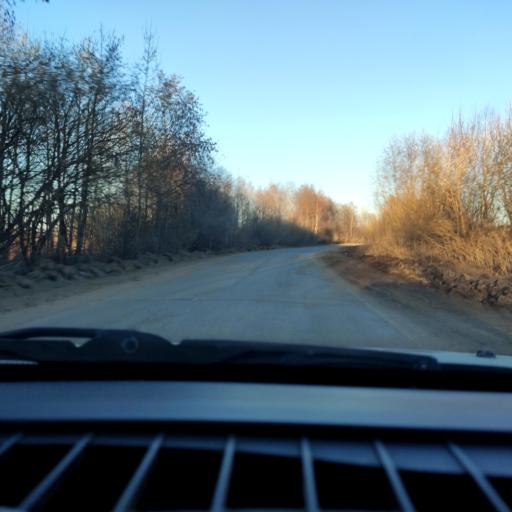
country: RU
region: Perm
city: Kultayevo
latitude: 57.9519
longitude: 55.9943
